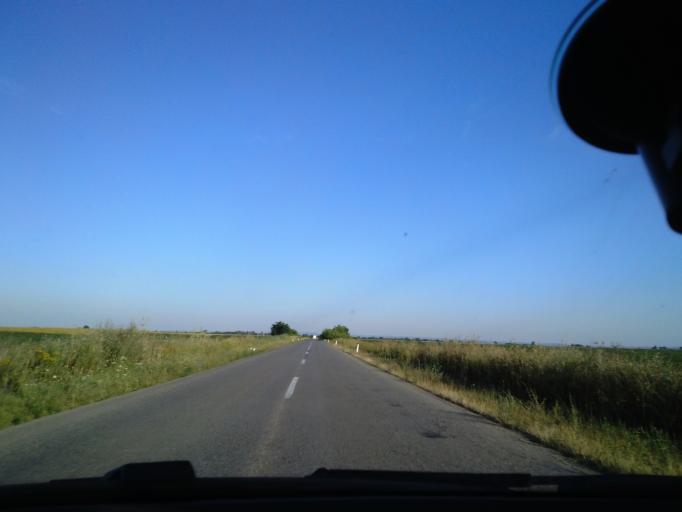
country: RS
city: Obrovac
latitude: 45.4343
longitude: 19.3779
